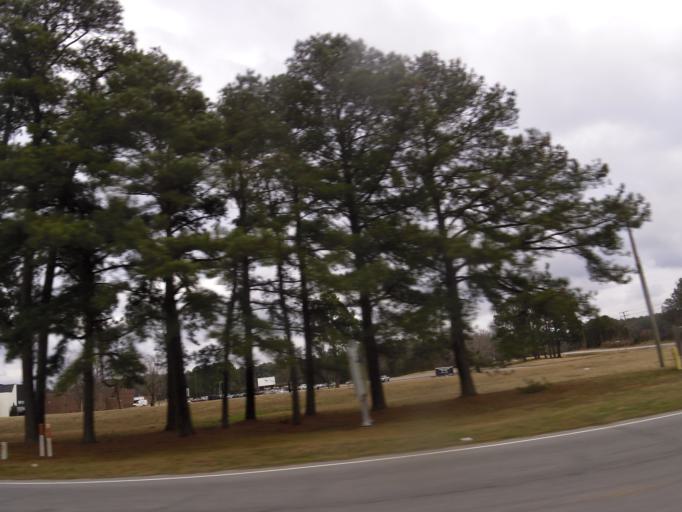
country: US
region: North Carolina
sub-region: Edgecombe County
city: Pinetops
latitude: 35.8347
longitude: -77.6602
